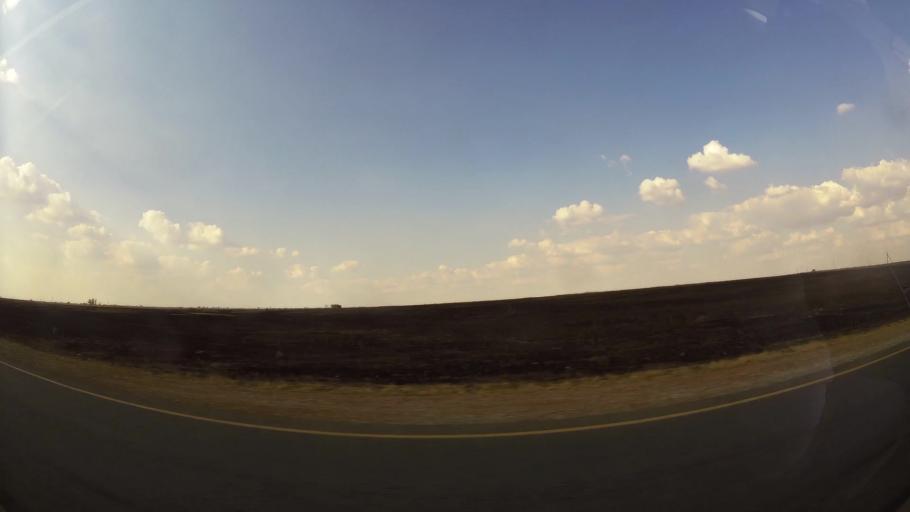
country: ZA
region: Gauteng
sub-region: Sedibeng District Municipality
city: Heidelberg
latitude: -26.3872
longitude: 28.3454
